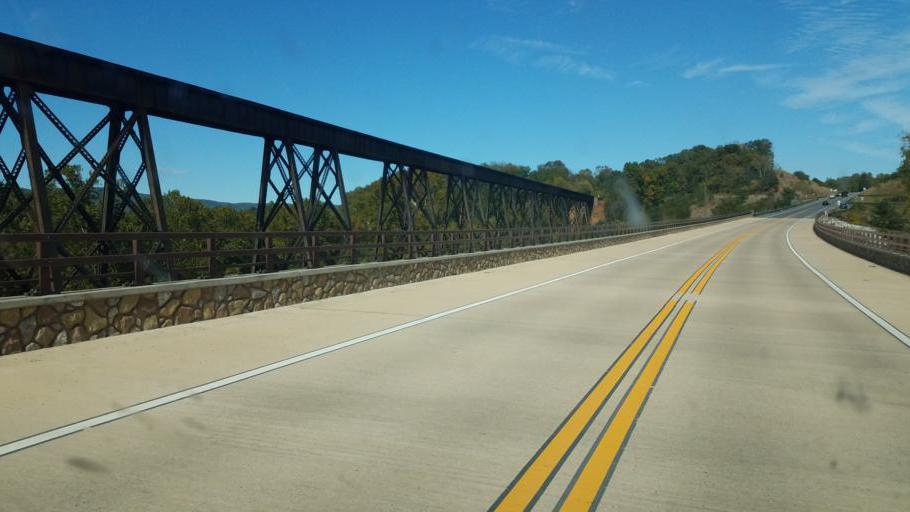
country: US
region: Virginia
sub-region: Page County
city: Luray
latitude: 38.7820
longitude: -78.3711
